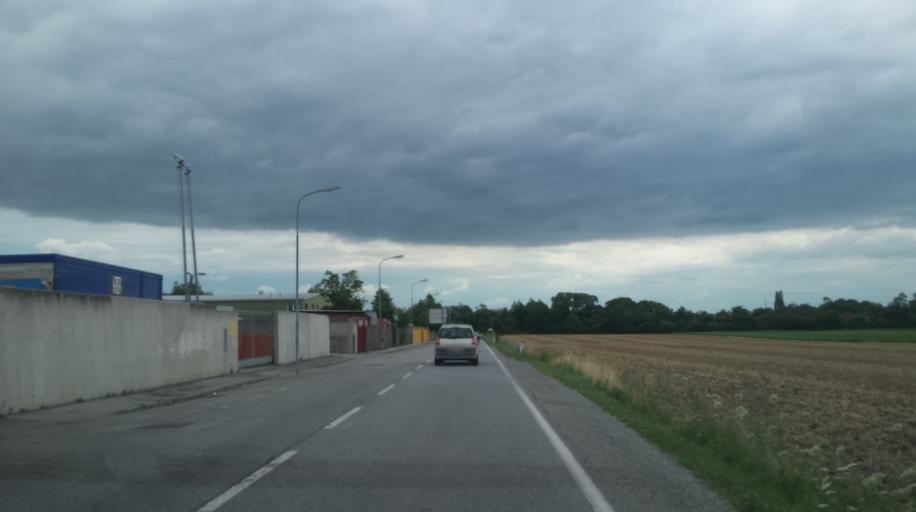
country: AT
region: Lower Austria
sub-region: Politischer Bezirk Wien-Umgebung
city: Zwolfaxing
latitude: 48.1168
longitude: 16.4549
